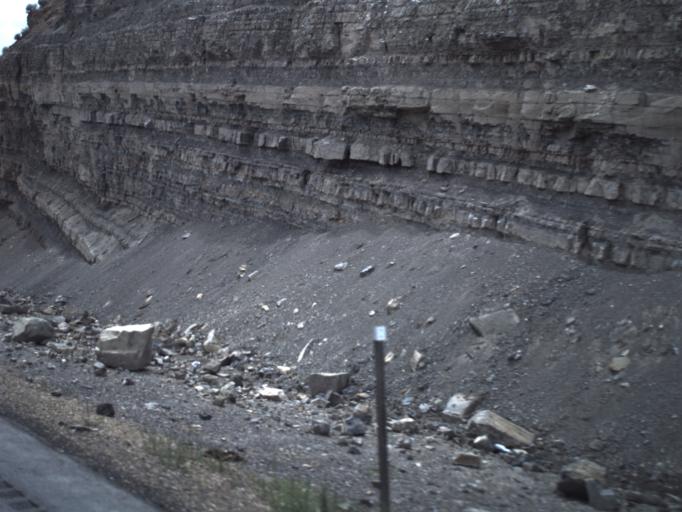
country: US
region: Utah
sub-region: Carbon County
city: Helper
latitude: 39.8141
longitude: -110.9390
